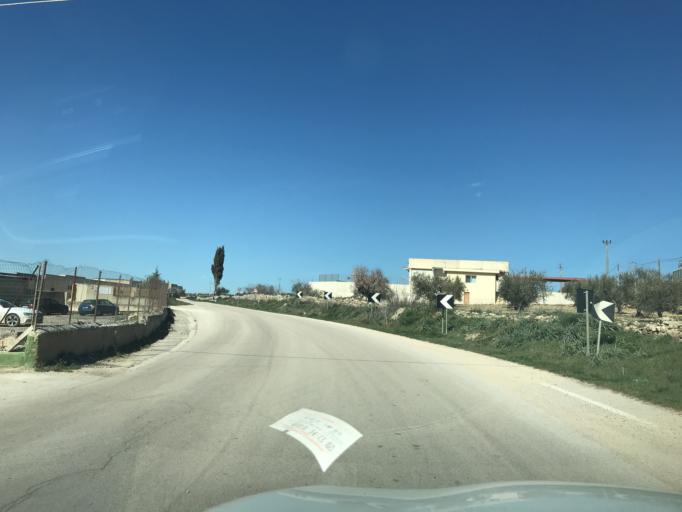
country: IT
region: Apulia
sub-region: Provincia di Bari
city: Gravina in Puglia
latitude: 40.8401
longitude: 16.4276
